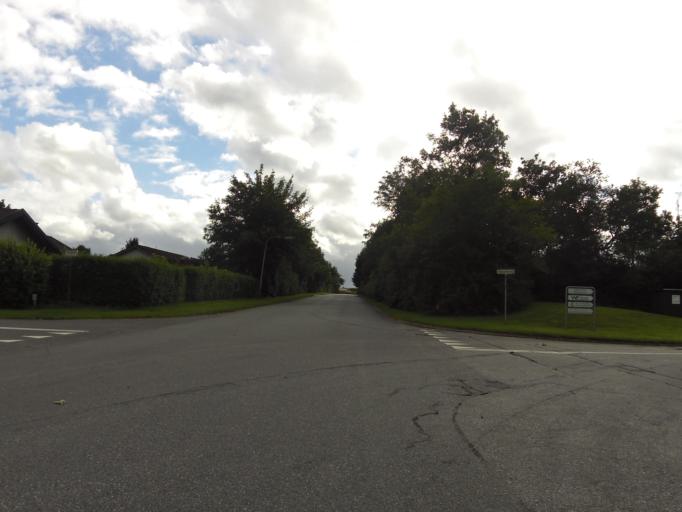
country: DK
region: South Denmark
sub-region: Tonder Kommune
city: Toftlund
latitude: 55.1339
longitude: 9.1247
